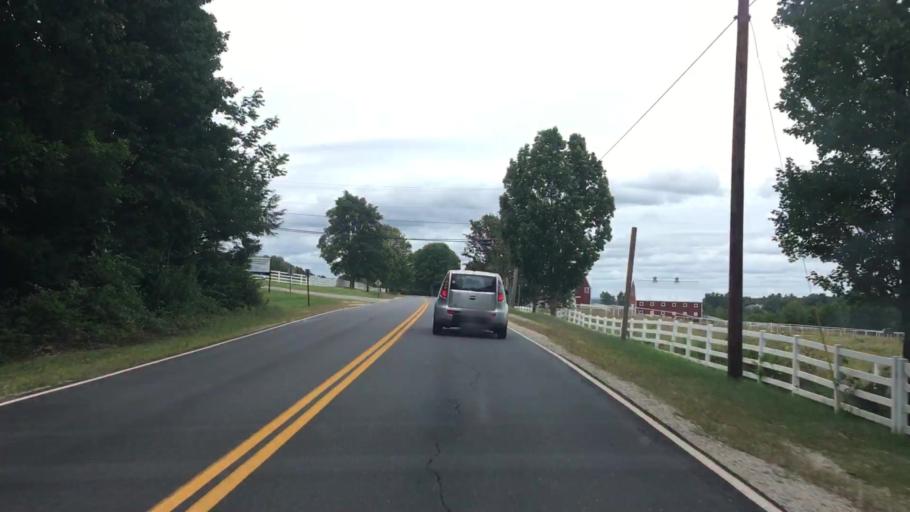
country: US
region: Maine
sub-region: Cumberland County
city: New Gloucester
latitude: 43.8925
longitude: -70.2535
